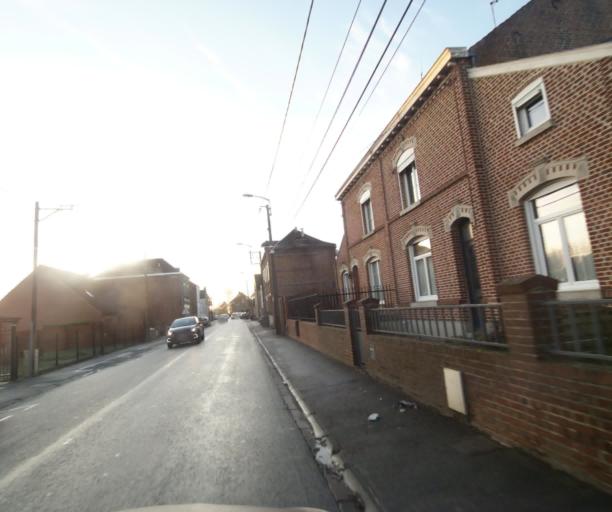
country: FR
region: Nord-Pas-de-Calais
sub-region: Departement du Nord
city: Onnaing
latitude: 50.3850
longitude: 3.6024
